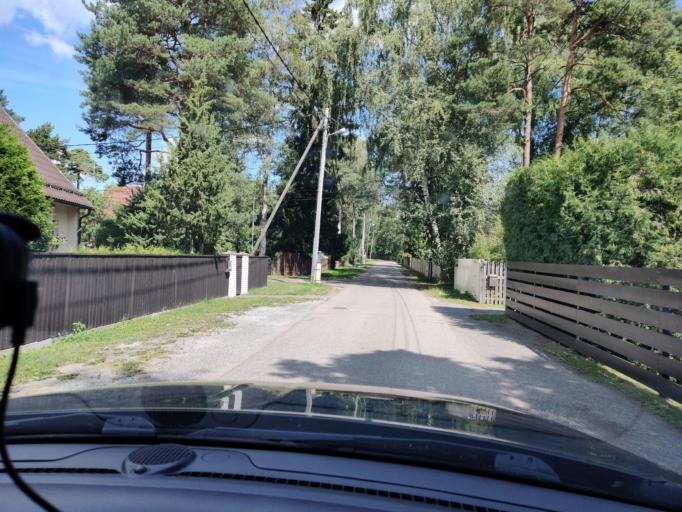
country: EE
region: Harju
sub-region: Saue vald
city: Laagri
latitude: 59.3760
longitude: 24.6388
